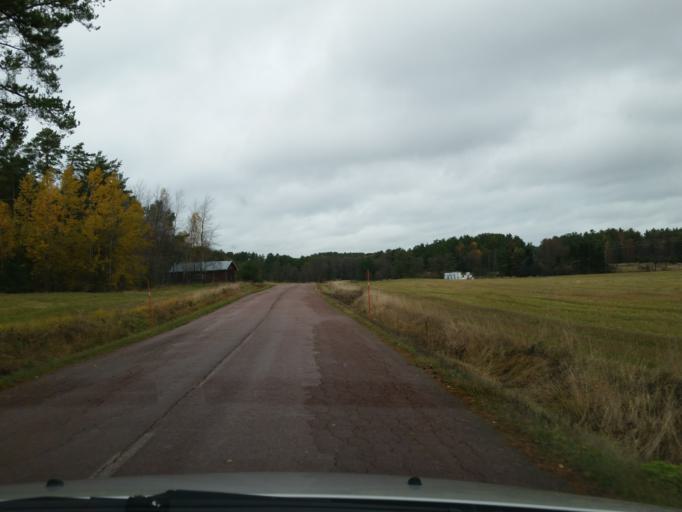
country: AX
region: Alands landsbygd
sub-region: Lumparland
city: Lumparland
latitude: 60.1280
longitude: 20.2425
